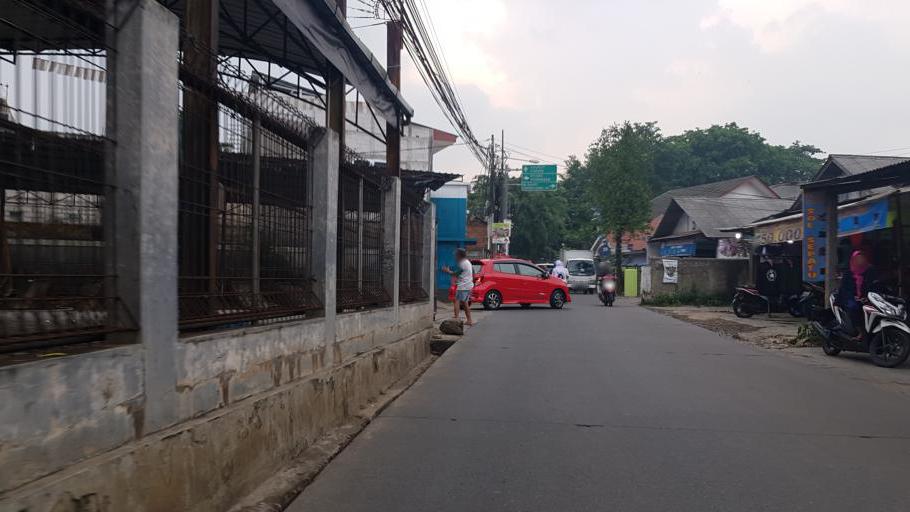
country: ID
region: West Java
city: Depok
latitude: -6.3687
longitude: 106.8089
